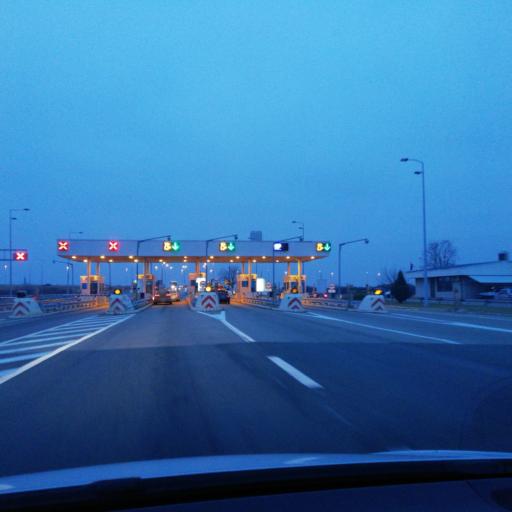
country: RS
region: Autonomna Pokrajina Vojvodina
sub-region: Sremski Okrug
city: Ruma
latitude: 44.9649
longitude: 19.8106
